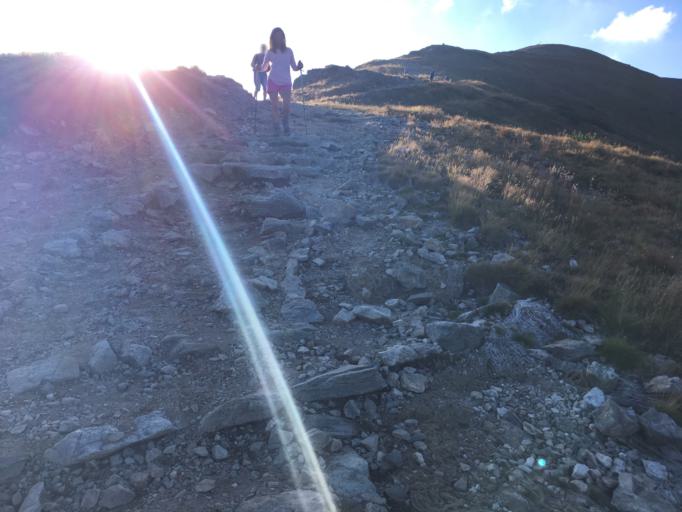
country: PL
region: Lesser Poland Voivodeship
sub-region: Powiat tatrzanski
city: Zakopane
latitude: 49.2347
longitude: 19.9364
